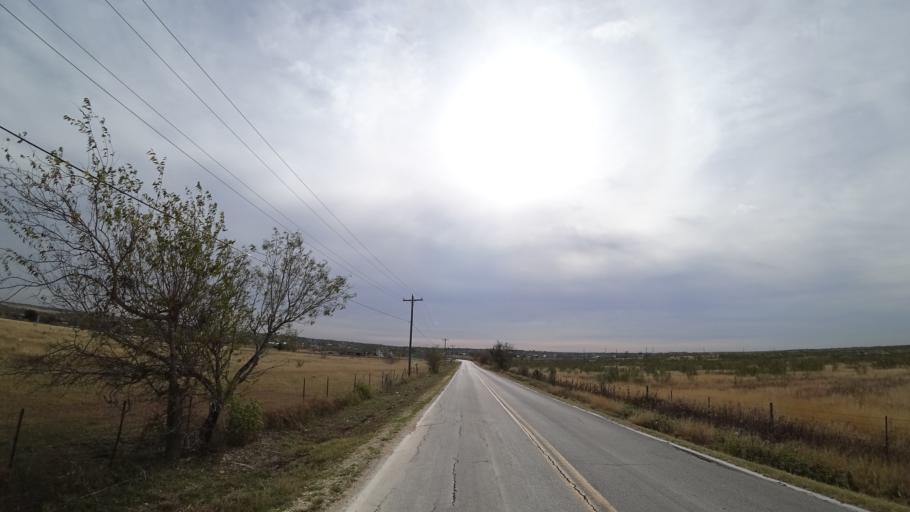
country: US
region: Texas
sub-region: Travis County
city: Garfield
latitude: 30.1267
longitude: -97.6005
